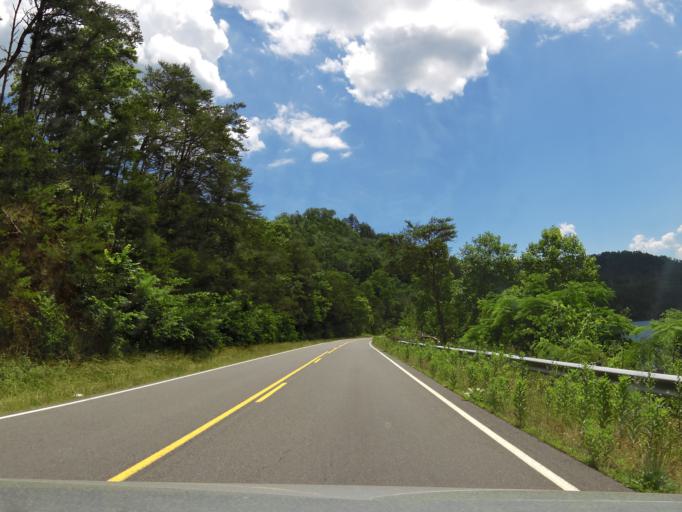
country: US
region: Tennessee
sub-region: Blount County
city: Maryville
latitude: 35.5550
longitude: -83.9973
